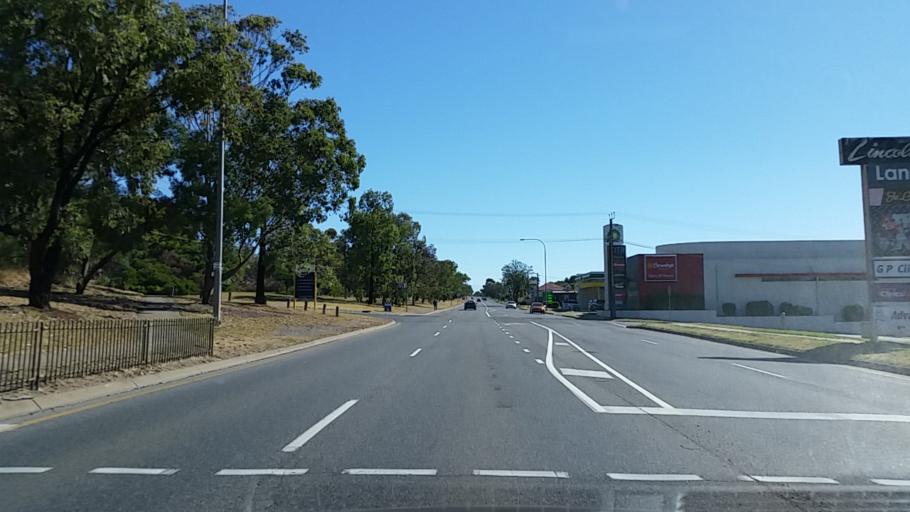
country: AU
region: South Australia
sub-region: Salisbury
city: Ingle Farm
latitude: -34.8276
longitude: 138.6327
